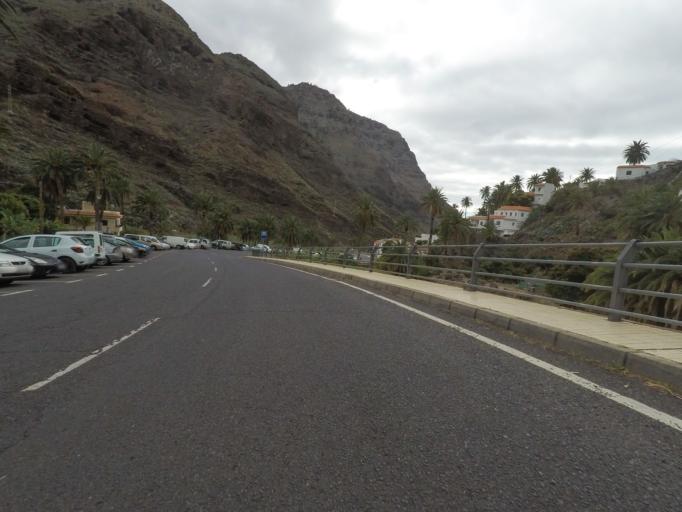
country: ES
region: Canary Islands
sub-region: Provincia de Santa Cruz de Tenerife
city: Vallehermosa
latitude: 28.1076
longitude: -17.3259
